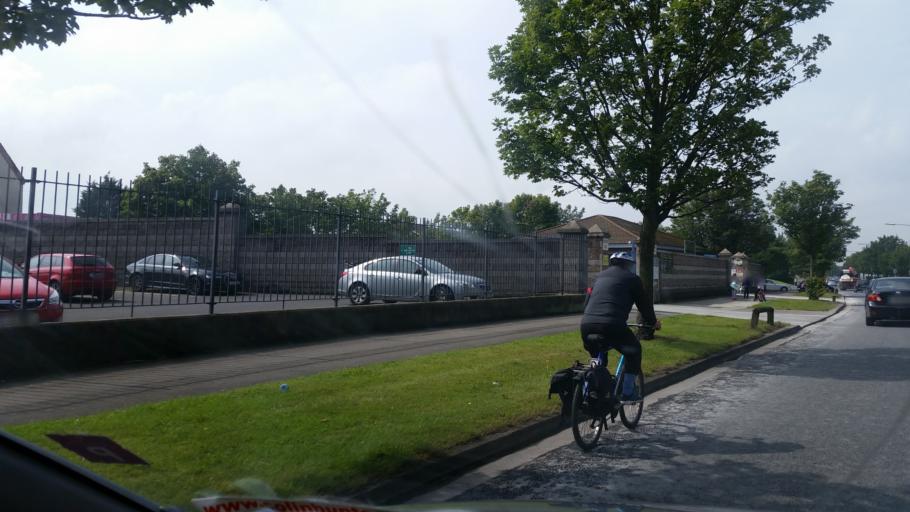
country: IE
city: Coolock
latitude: 53.3907
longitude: -6.2011
